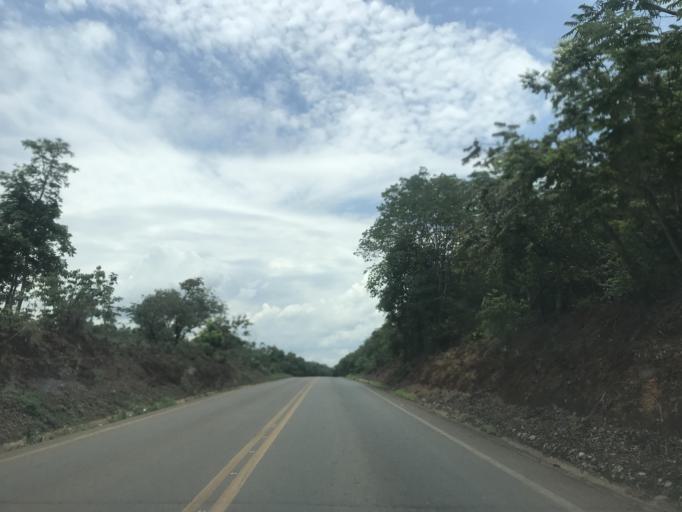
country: BR
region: Goias
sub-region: Vianopolis
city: Vianopolis
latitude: -16.7228
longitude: -48.4097
